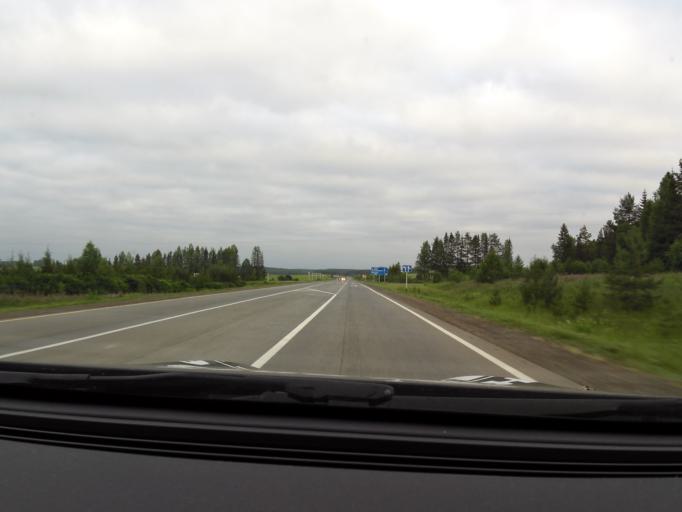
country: RU
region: Perm
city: Siva
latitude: 58.4227
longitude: 54.4560
